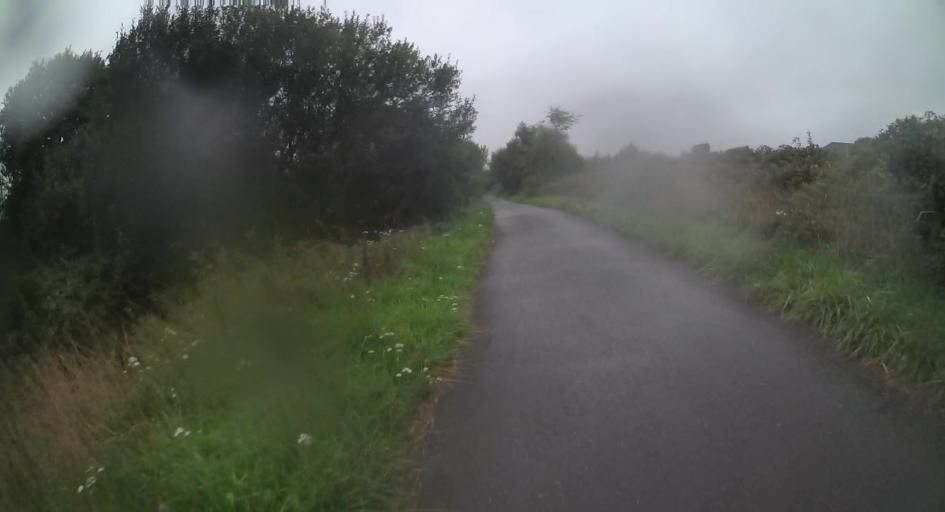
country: GB
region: England
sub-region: Isle of Wight
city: Newchurch
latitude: 50.6678
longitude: -1.2223
